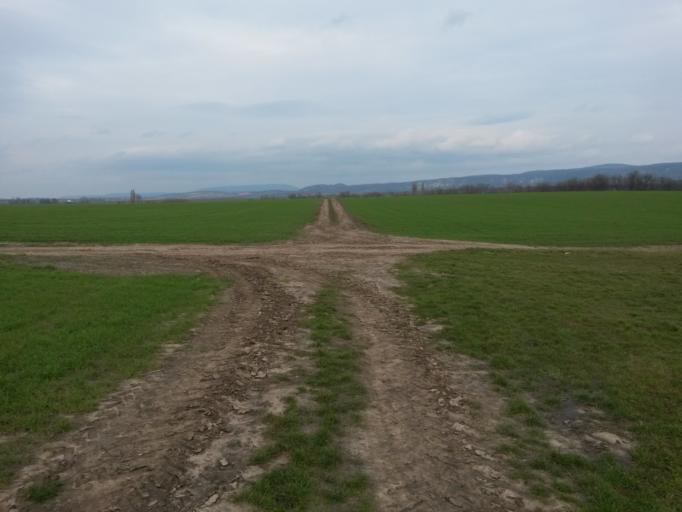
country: HU
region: Pest
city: Perbal
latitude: 47.5562
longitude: 18.7588
